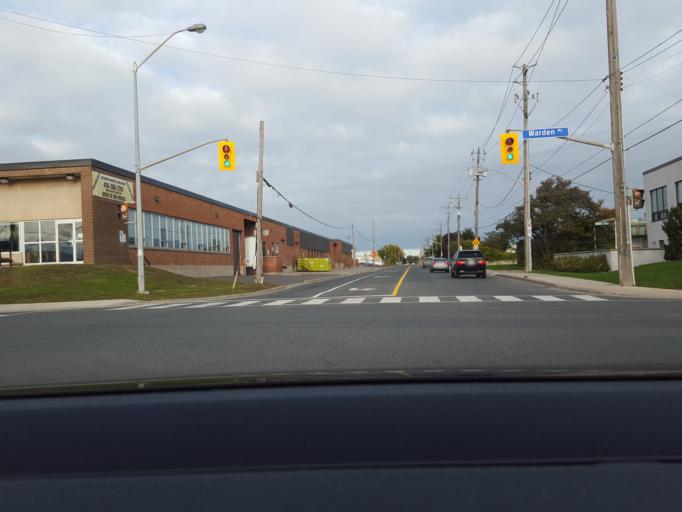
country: CA
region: Ontario
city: Scarborough
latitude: 43.7215
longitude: -79.2851
